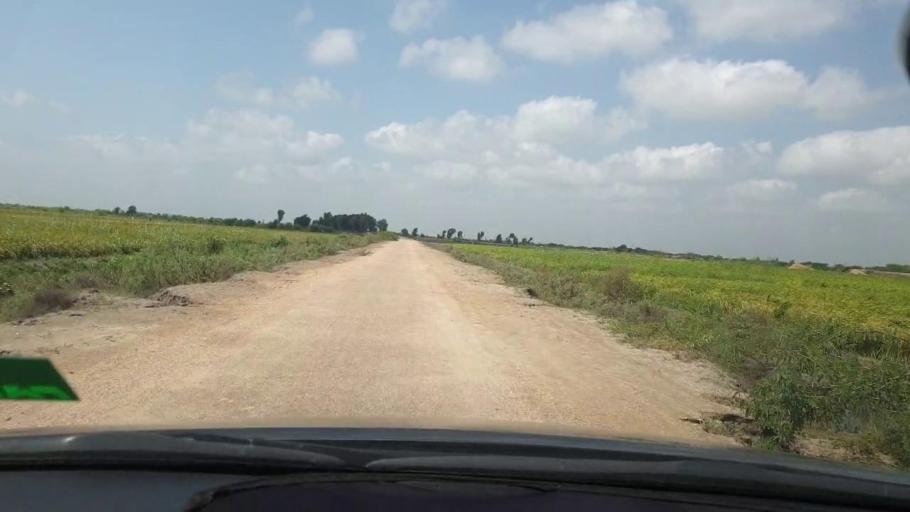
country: PK
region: Sindh
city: Tando Bago
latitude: 24.8723
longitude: 69.0352
